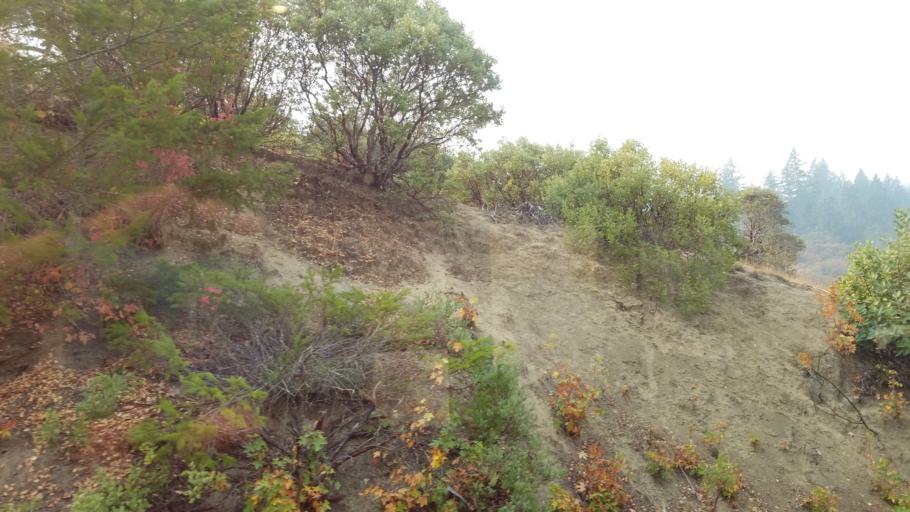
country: US
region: California
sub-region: Mendocino County
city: Willits
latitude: 39.4033
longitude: -123.3907
